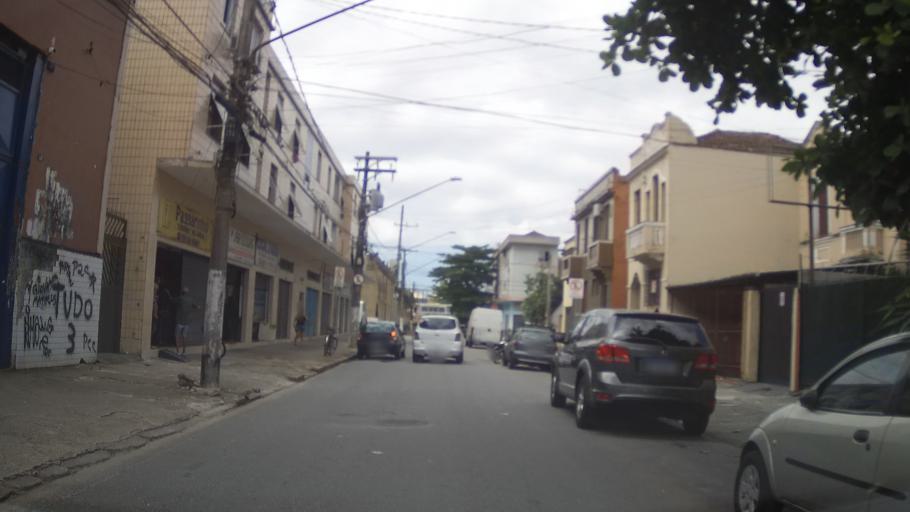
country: BR
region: Sao Paulo
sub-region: Santos
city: Santos
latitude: -23.9552
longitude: -46.3165
